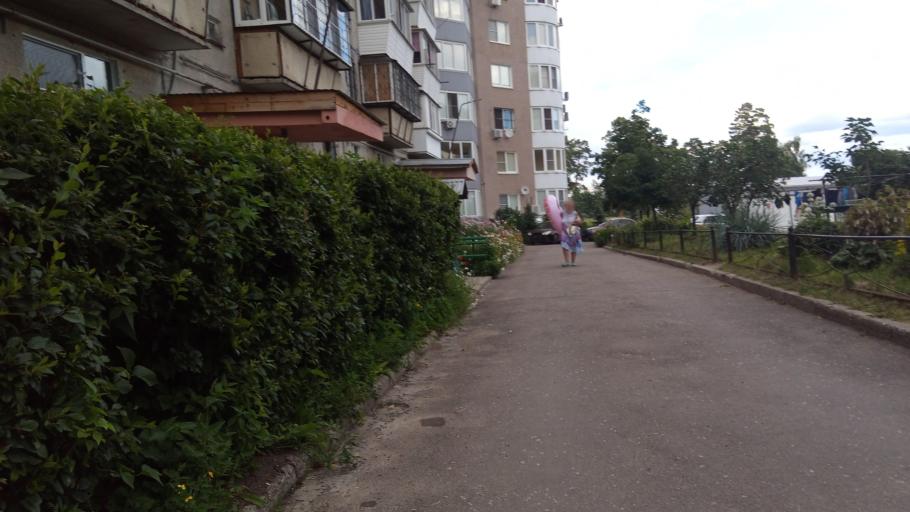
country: RU
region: Chelyabinsk
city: Chebarkul'
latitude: 55.0207
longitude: 60.3120
